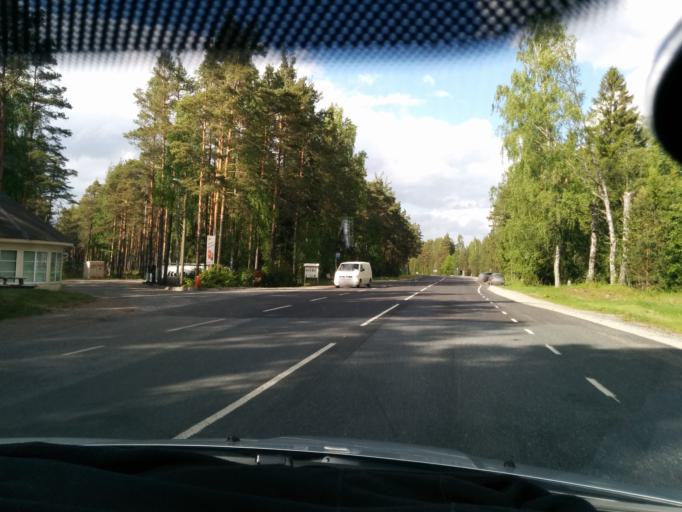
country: EE
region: Harju
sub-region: Loksa linn
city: Loksa
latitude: 59.5396
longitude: 25.7341
